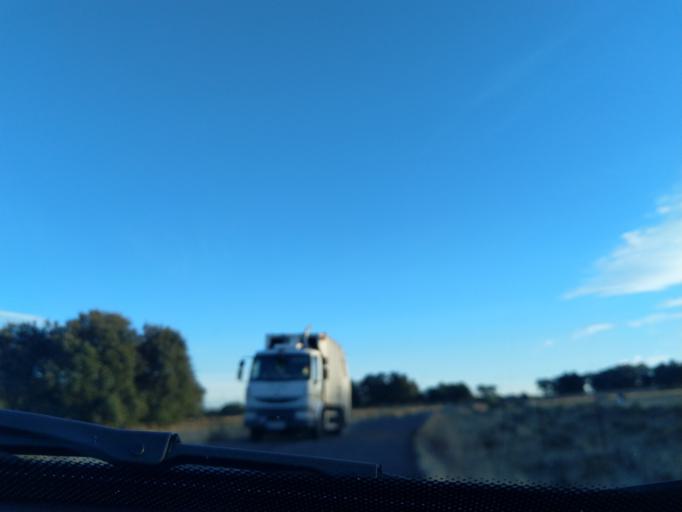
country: ES
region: Extremadura
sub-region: Provincia de Badajoz
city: Valverde de Llerena
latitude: 38.2346
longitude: -5.8225
